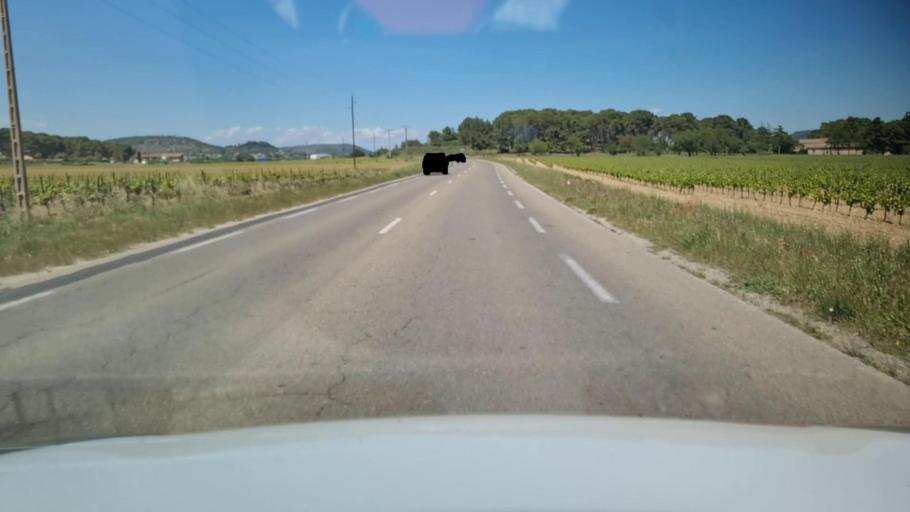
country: FR
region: Languedoc-Roussillon
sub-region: Departement du Gard
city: Mus
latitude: 43.7567
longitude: 4.2046
